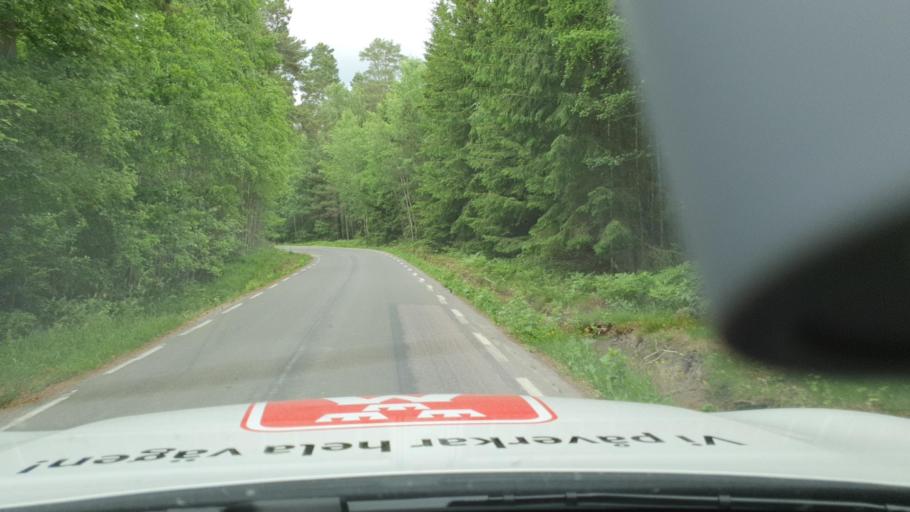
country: SE
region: Vaestra Goetaland
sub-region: Tidaholms Kommun
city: Olofstorp
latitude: 58.2849
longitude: 14.1026
